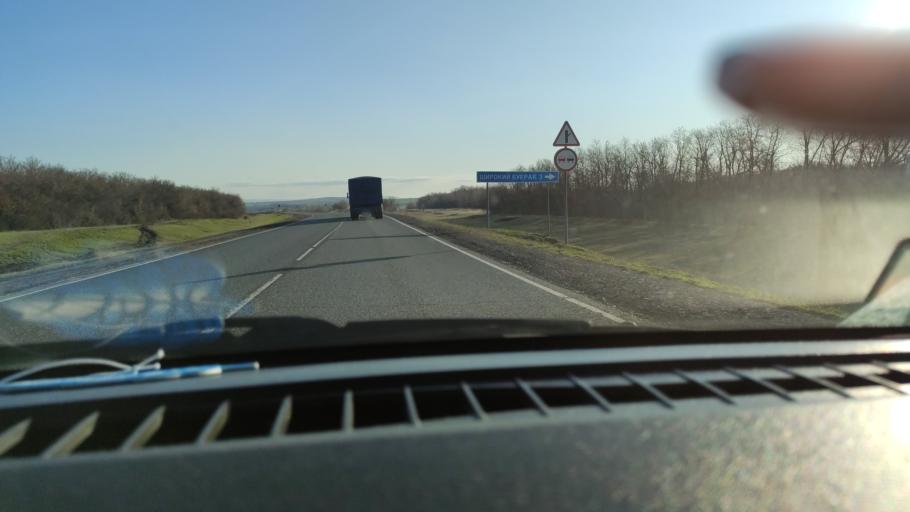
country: RU
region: Saratov
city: Balakovo
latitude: 52.1064
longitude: 47.7436
